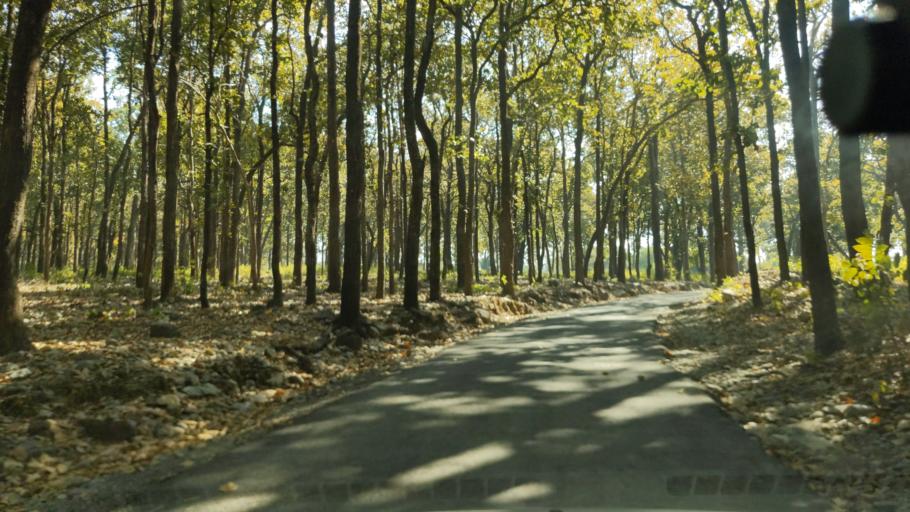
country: IN
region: Uttarakhand
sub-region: Naini Tal
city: Ramnagar
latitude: 29.4692
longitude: 79.2346
